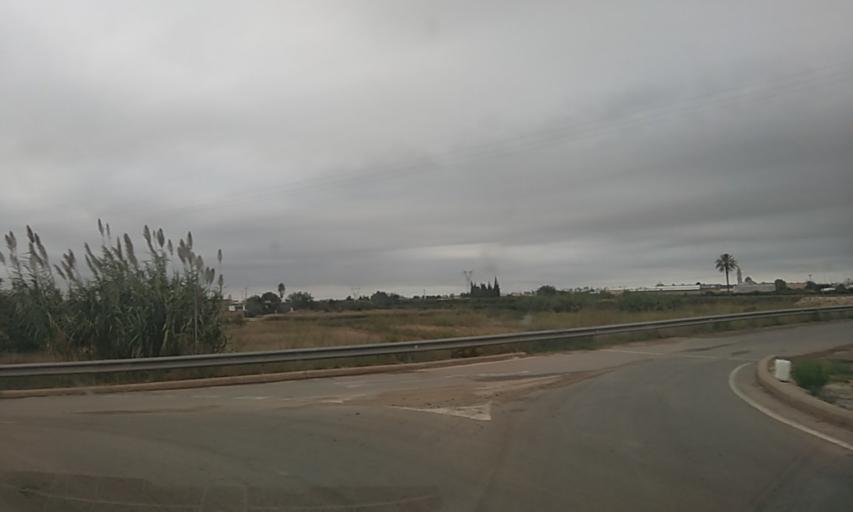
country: ES
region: Valencia
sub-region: Provincia de Valencia
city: L'Alcudia
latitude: 39.1895
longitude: -0.5215
